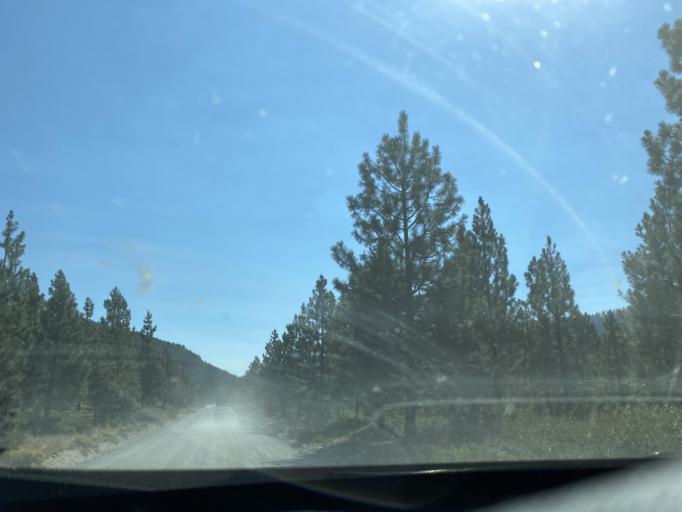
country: US
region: Oregon
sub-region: Deschutes County
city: Sunriver
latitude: 44.0345
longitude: -121.5344
